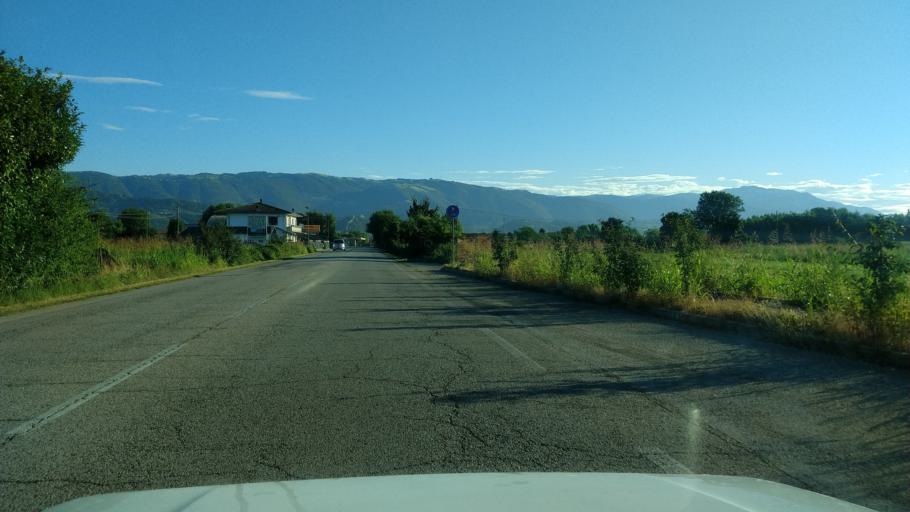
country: IT
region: Veneto
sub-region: Provincia di Vicenza
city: Schiavon
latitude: 45.7153
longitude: 11.6498
